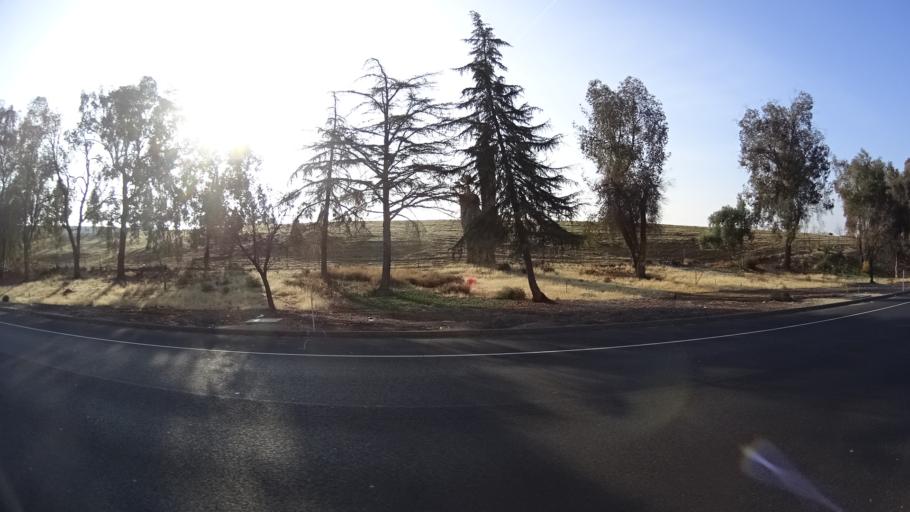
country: US
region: California
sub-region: Kern County
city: Bakersfield
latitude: 35.3953
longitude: -118.9645
